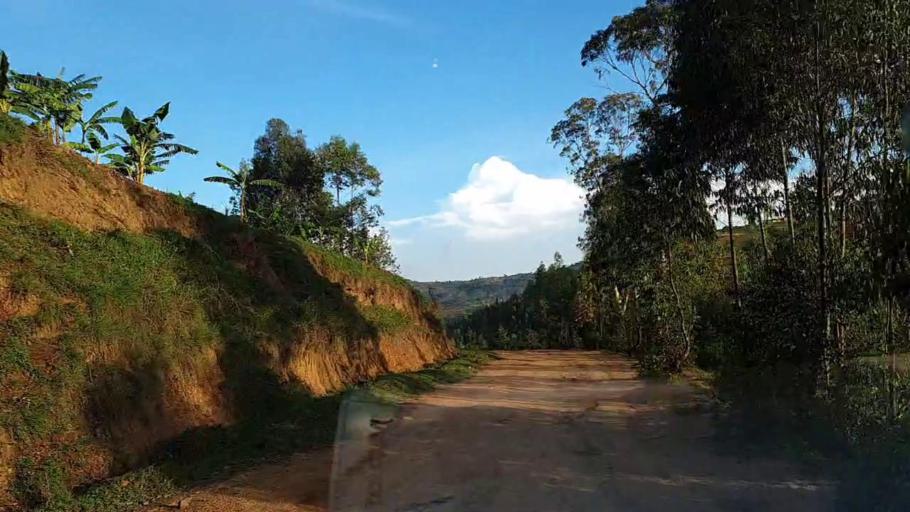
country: RW
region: Southern Province
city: Gikongoro
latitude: -2.3964
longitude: 29.5555
